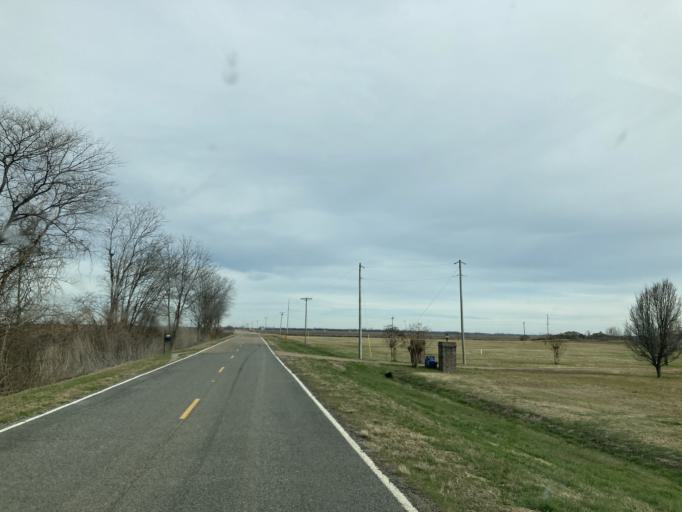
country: US
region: Mississippi
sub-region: Humphreys County
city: Belzoni
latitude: 33.1675
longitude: -90.5579
